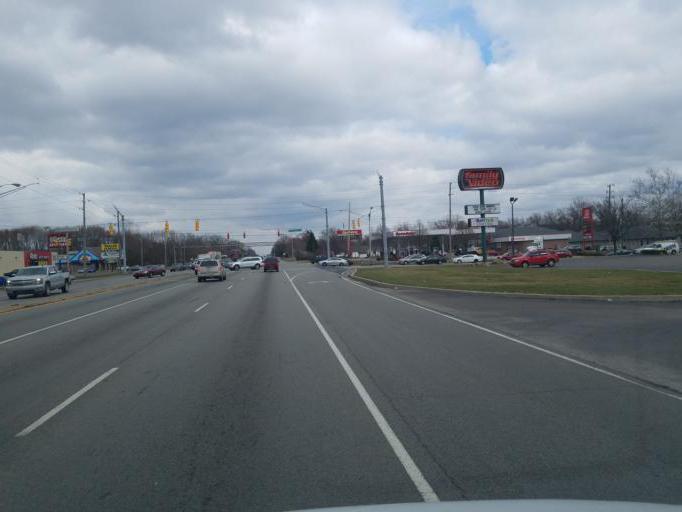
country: US
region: Indiana
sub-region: Marion County
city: Speedway
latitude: 39.7642
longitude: -86.2901
